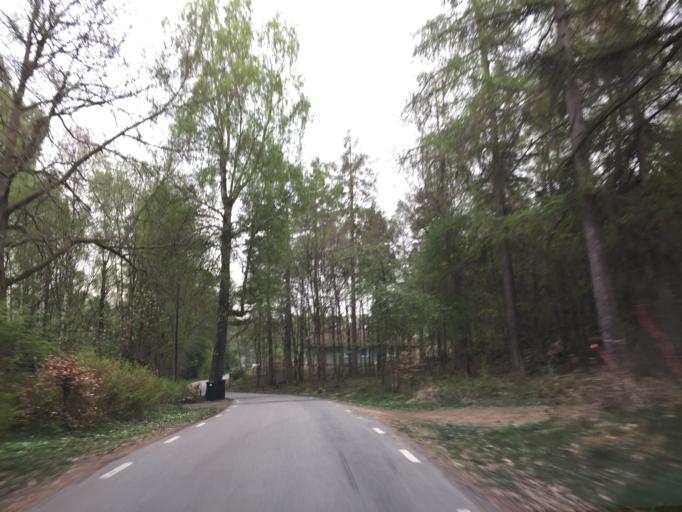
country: SE
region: Vaestra Goetaland
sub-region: Ale Kommun
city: Surte
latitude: 57.8404
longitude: 11.9939
